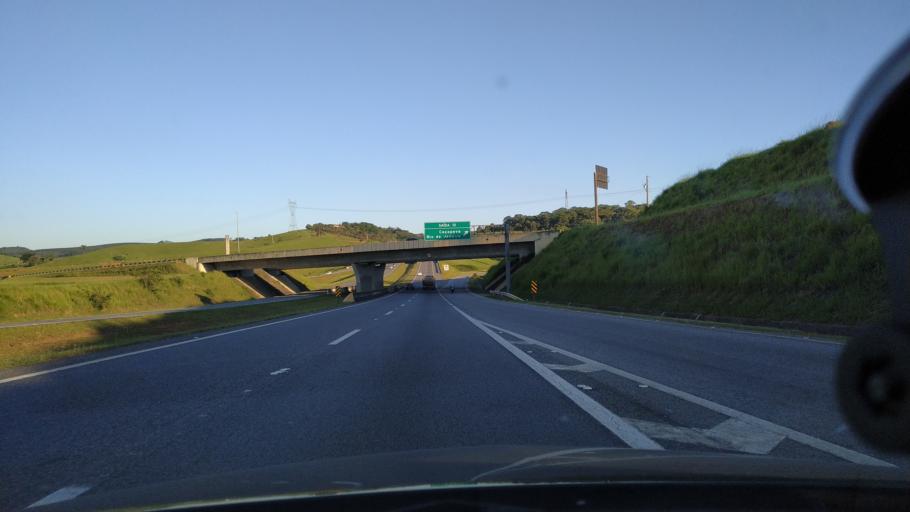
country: BR
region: Sao Paulo
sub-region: Sao Jose Dos Campos
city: Sao Jose dos Campos
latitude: -23.2666
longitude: -45.8218
